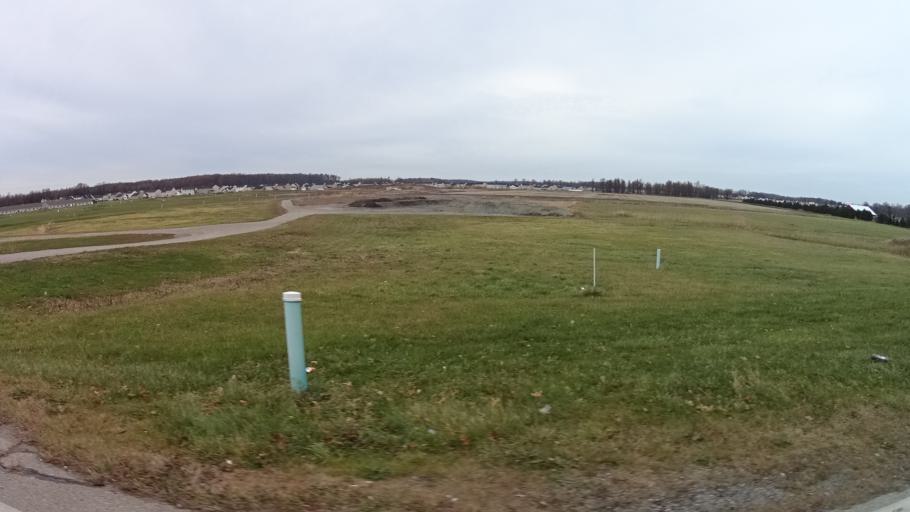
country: US
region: Ohio
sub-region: Lorain County
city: North Ridgeville
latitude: 41.3854
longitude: -82.0365
